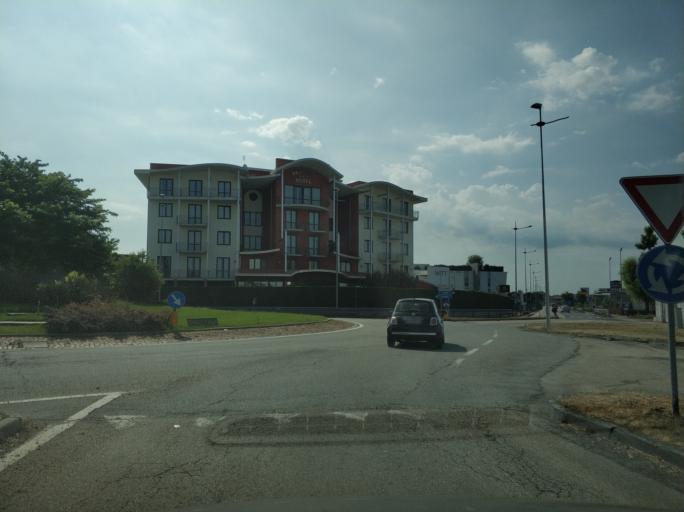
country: IT
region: Piedmont
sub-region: Provincia di Torino
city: Poirino
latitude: 44.9282
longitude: 7.8351
